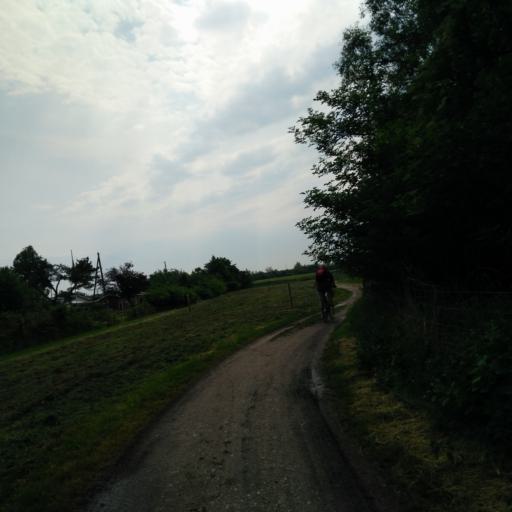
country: DK
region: Capital Region
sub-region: Ballerup Kommune
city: Ballerup
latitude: 55.7108
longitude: 12.3756
